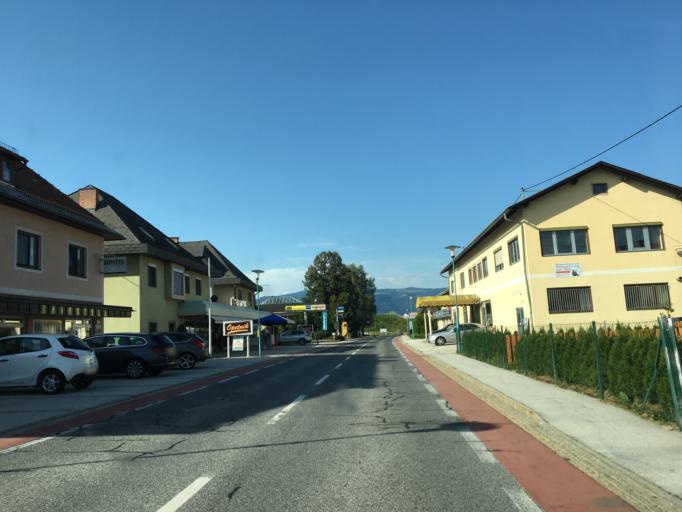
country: AT
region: Carinthia
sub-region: Politischer Bezirk Volkermarkt
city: Eberndorf
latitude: 46.6237
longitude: 14.6335
